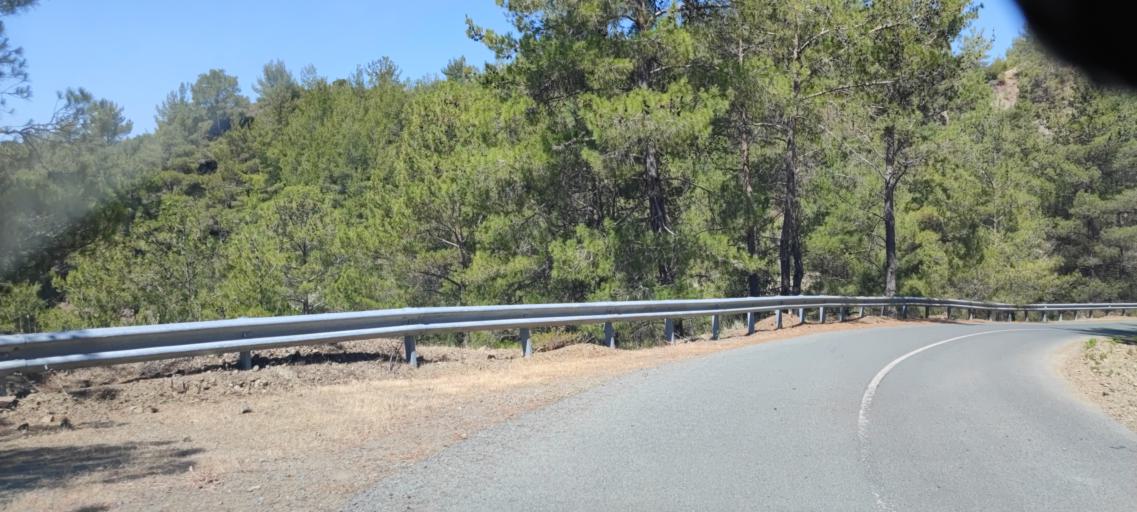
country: CY
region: Lefkosia
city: Kakopetria
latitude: 34.9248
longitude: 32.8000
